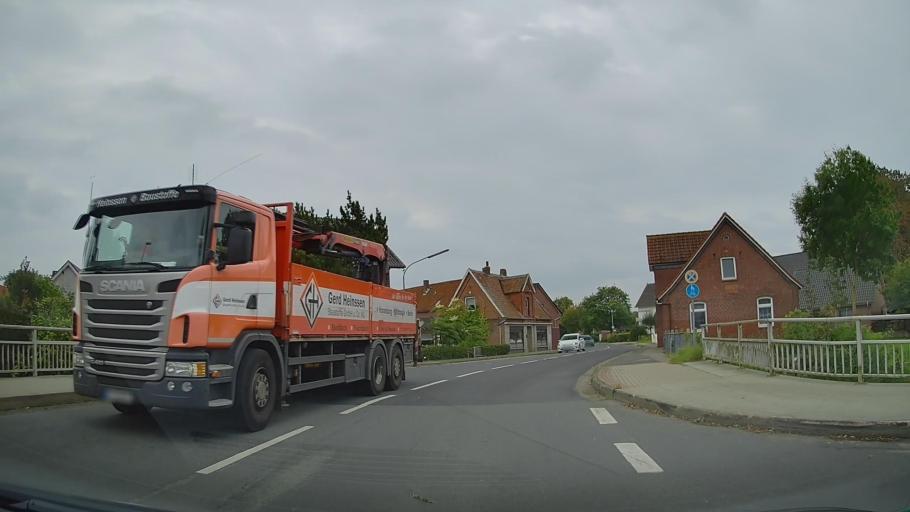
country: DE
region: Lower Saxony
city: Freiburg
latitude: 53.8239
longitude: 9.2879
